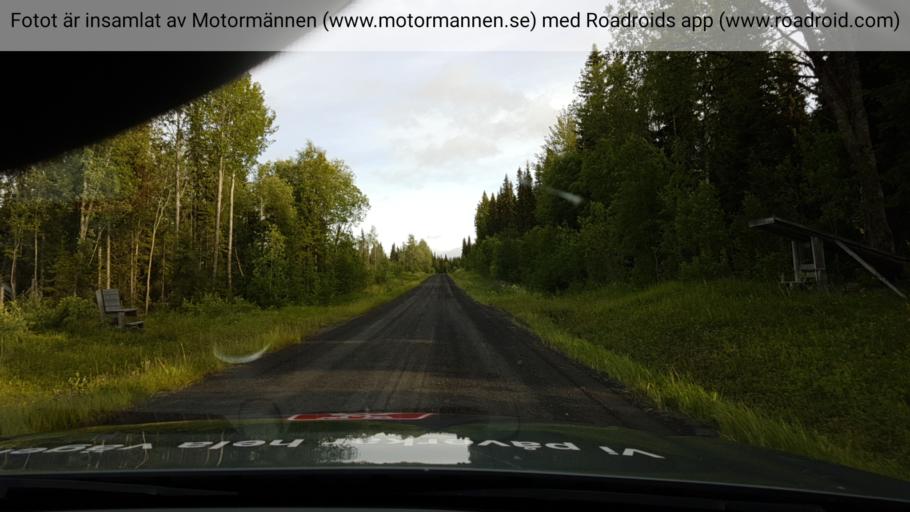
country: SE
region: Jaemtland
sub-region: OEstersunds Kommun
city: Lit
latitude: 63.6491
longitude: 15.0722
